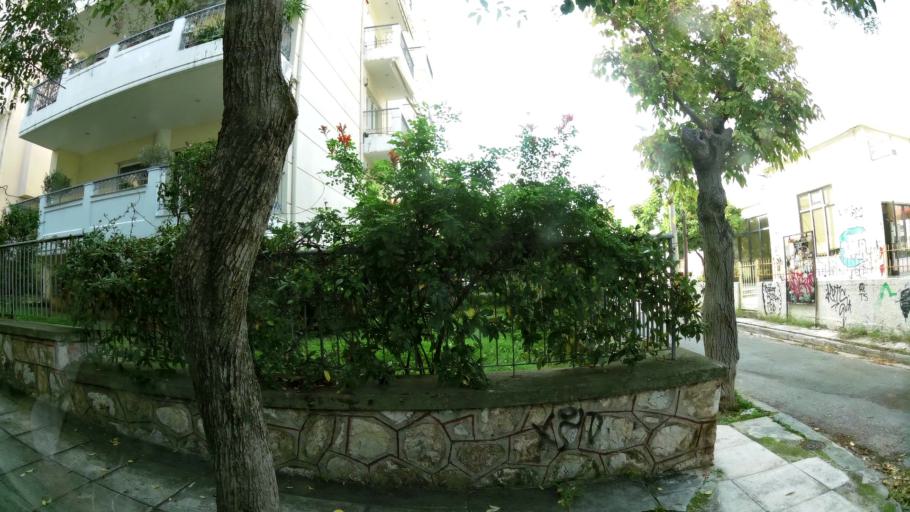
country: GR
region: Attica
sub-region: Nomarchia Athinas
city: Papagou
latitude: 37.9909
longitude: 23.7992
